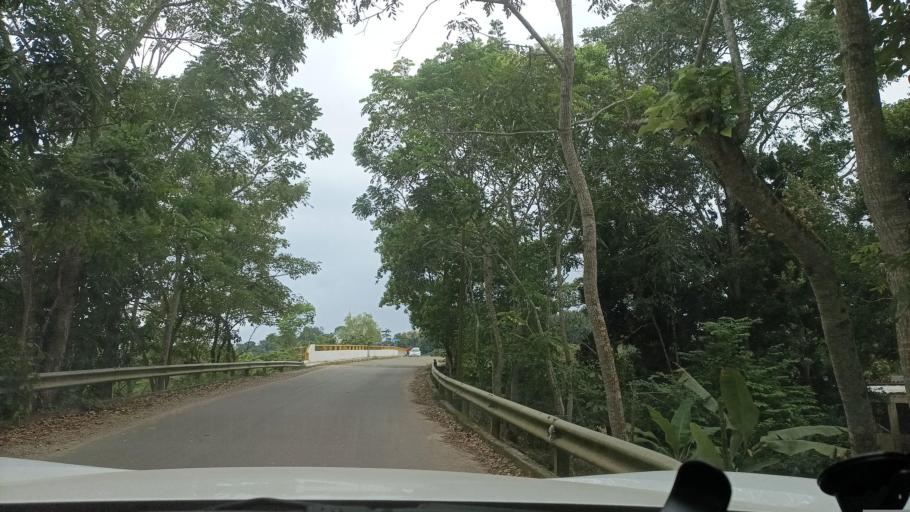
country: MX
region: Veracruz
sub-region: Jaltipan
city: Las Lomas de Tacamichapan
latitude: 17.8700
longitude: -94.7069
